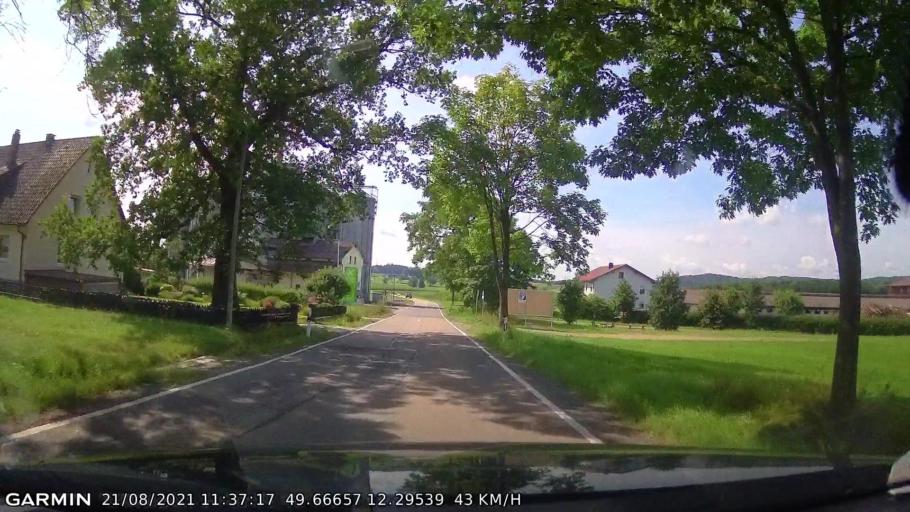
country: DE
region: Bavaria
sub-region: Upper Palatinate
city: Waldthurn
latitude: 49.6666
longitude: 12.2955
